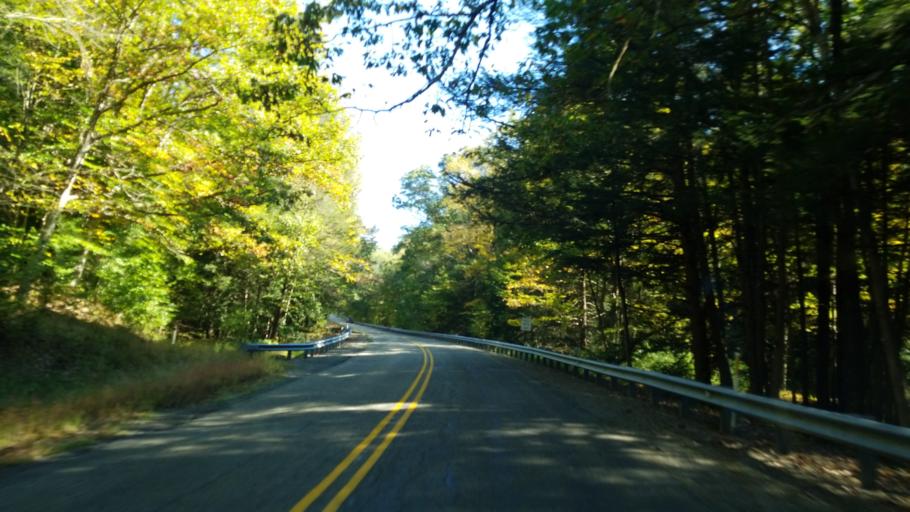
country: US
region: Pennsylvania
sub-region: Elk County
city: Saint Marys
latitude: 41.2669
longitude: -78.4025
